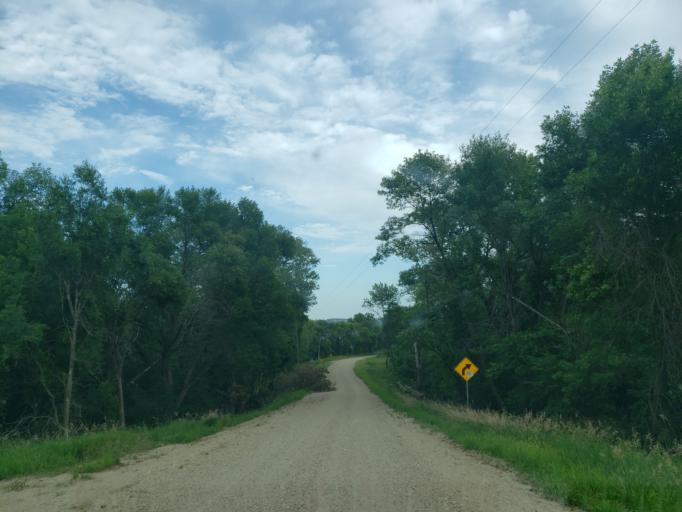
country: US
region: South Dakota
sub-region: Davison County
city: Mitchell
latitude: 43.6847
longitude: -97.9685
